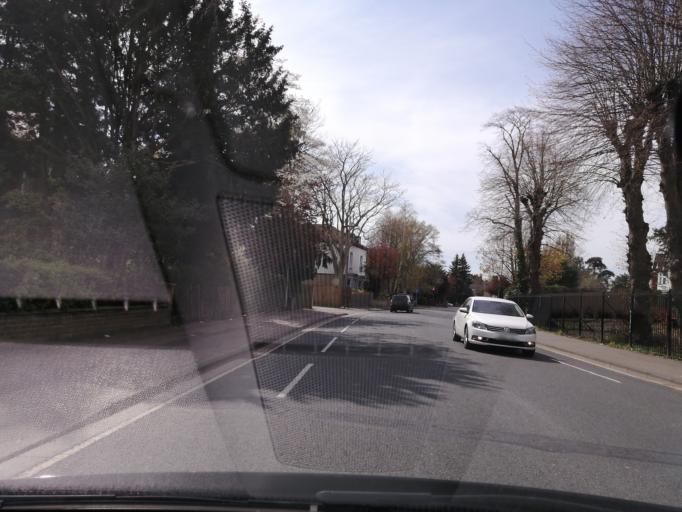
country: GB
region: England
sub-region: Peterborough
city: Peterborough
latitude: 52.5846
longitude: -0.2273
